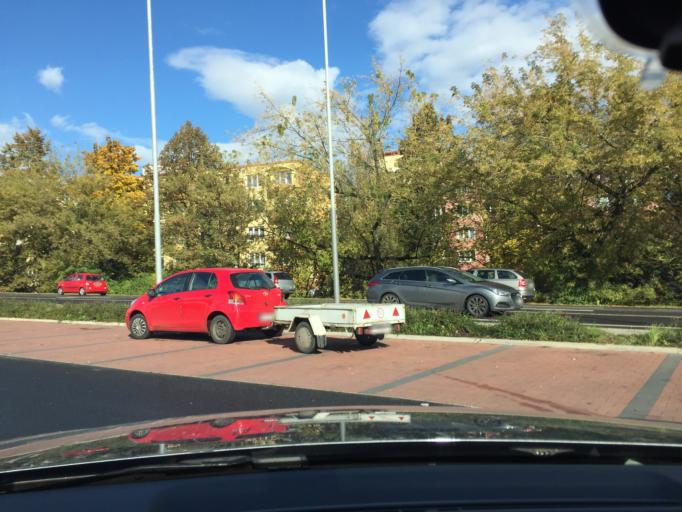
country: CZ
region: Ustecky
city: Trmice
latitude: 50.6845
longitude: 13.9949
